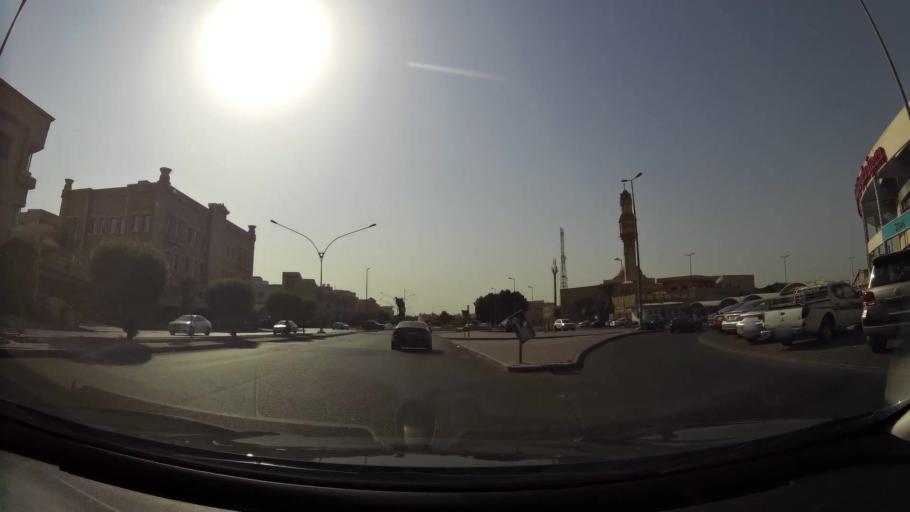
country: KW
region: Muhafazat Hawalli
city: Salwa
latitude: 29.2962
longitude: 48.0775
